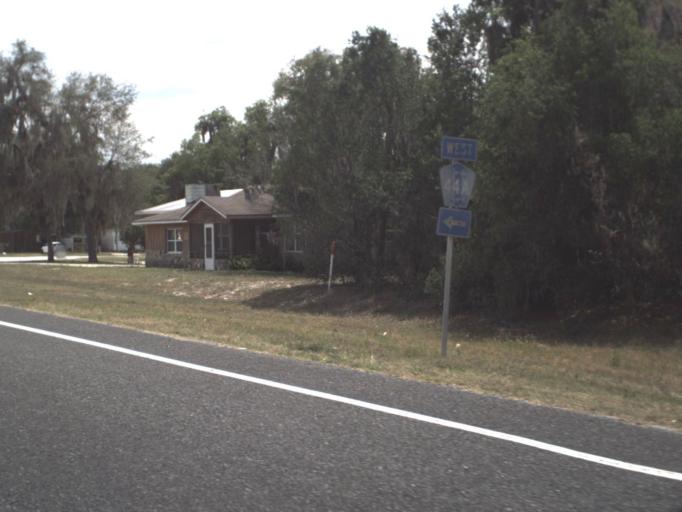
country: US
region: Florida
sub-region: Sumter County
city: Wildwood
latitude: 28.8316
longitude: -81.9991
